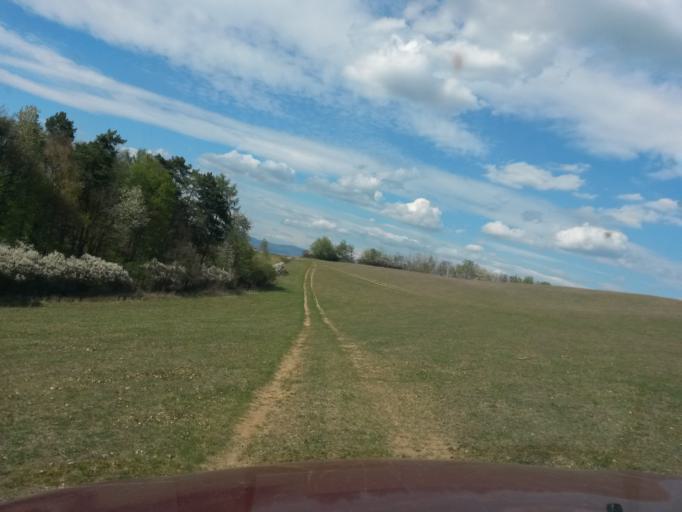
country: SK
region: Presovsky
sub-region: Okres Presov
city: Presov
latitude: 48.9497
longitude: 21.1239
